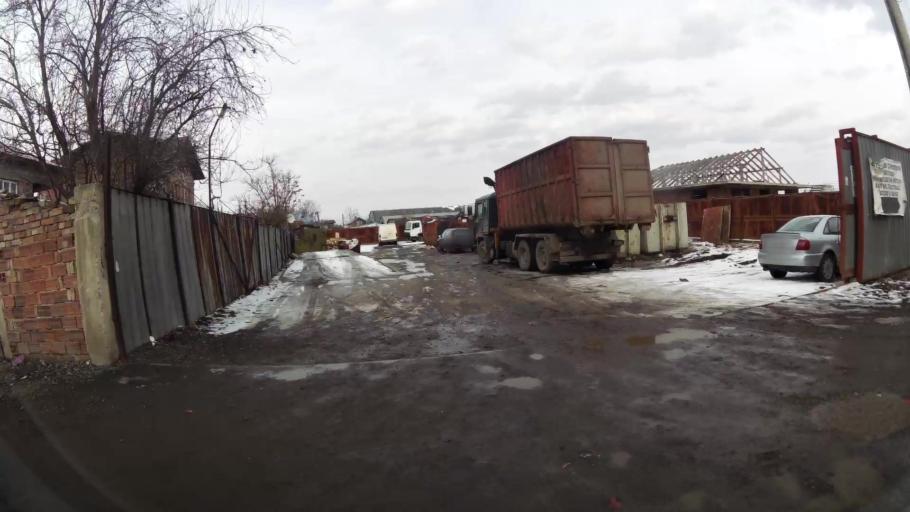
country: BG
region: Sofia-Capital
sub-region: Stolichna Obshtina
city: Sofia
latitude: 42.6943
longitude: 23.3834
